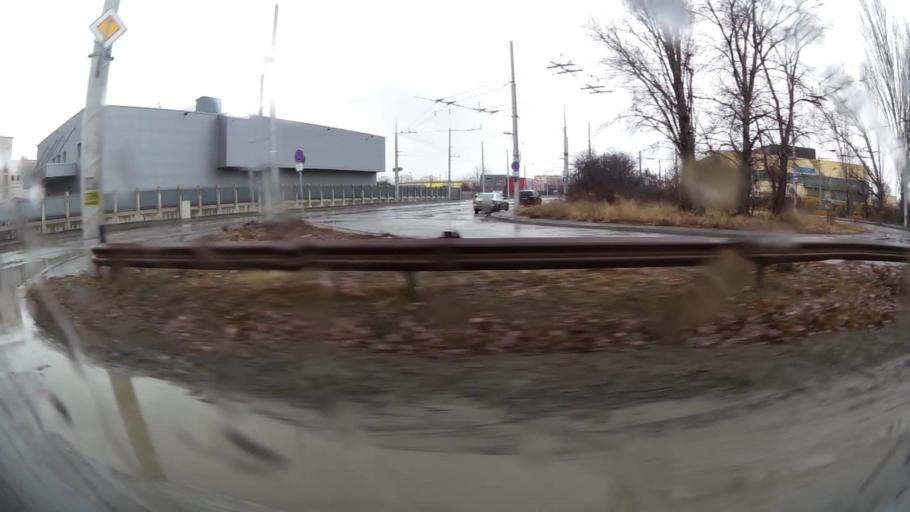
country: BG
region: Sofia-Capital
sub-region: Stolichna Obshtina
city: Sofia
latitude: 42.6535
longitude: 23.4142
